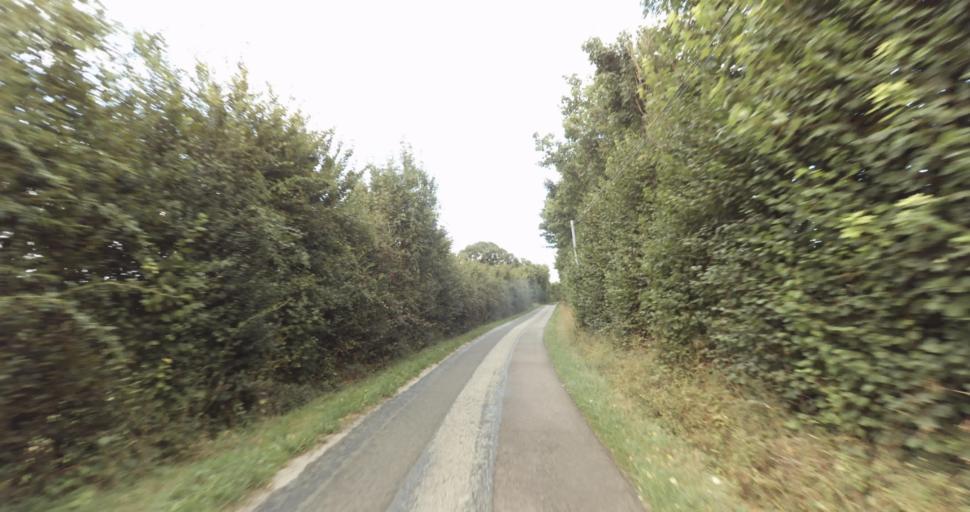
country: FR
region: Lower Normandy
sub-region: Departement de l'Orne
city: Gace
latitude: 48.7719
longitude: 0.3473
